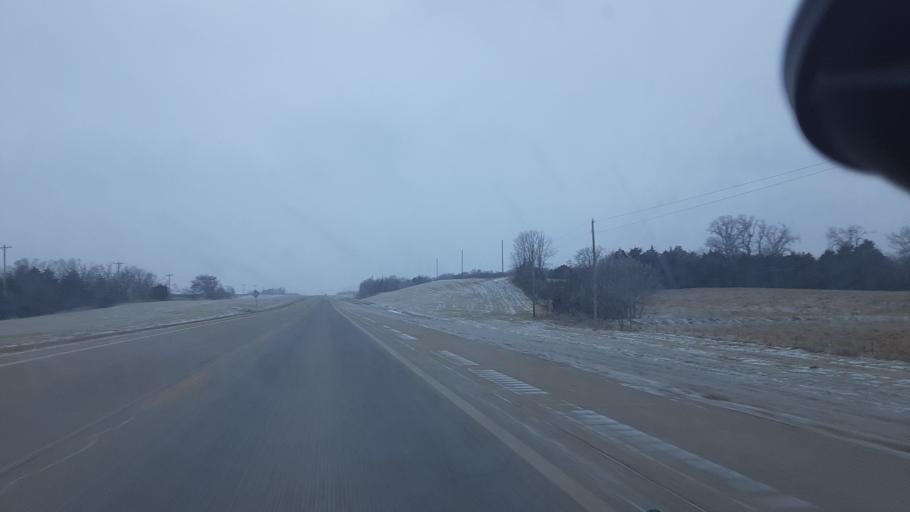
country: US
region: Oklahoma
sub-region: Payne County
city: Perkins
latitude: 35.9860
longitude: -97.1232
